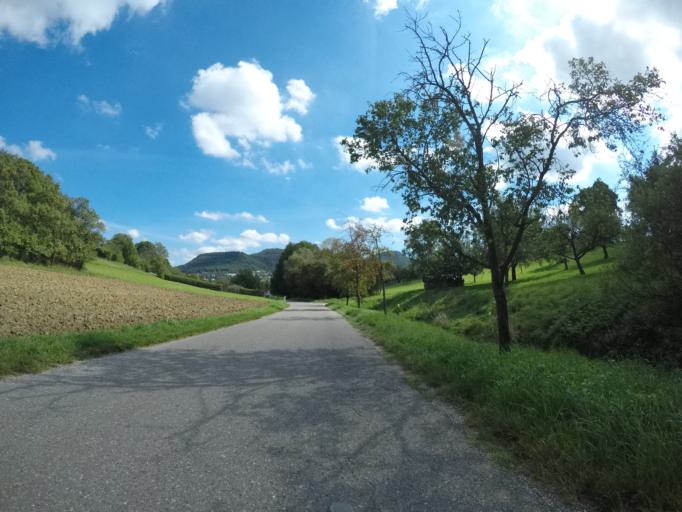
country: DE
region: Baden-Wuerttemberg
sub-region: Tuebingen Region
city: Pfullingen
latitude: 48.4548
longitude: 9.1992
